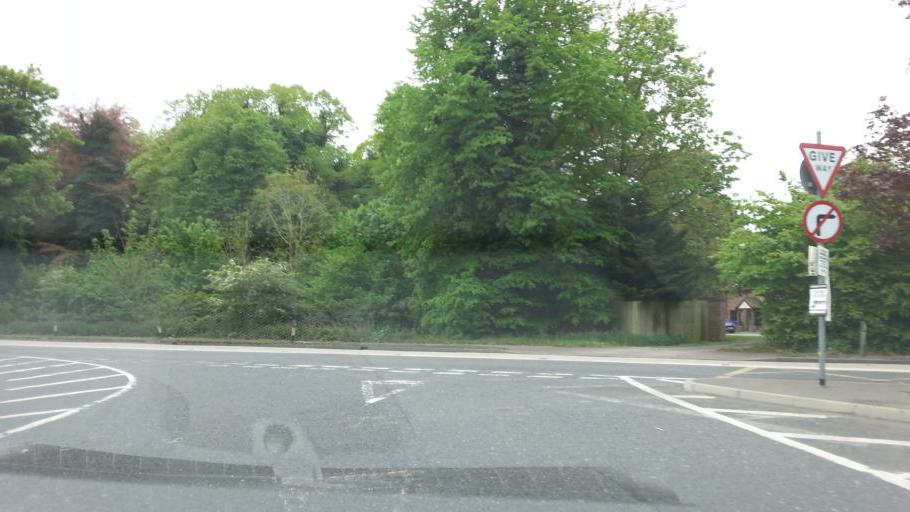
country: GB
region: England
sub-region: Suffolk
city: Lakenheath
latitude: 52.3385
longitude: 0.5330
